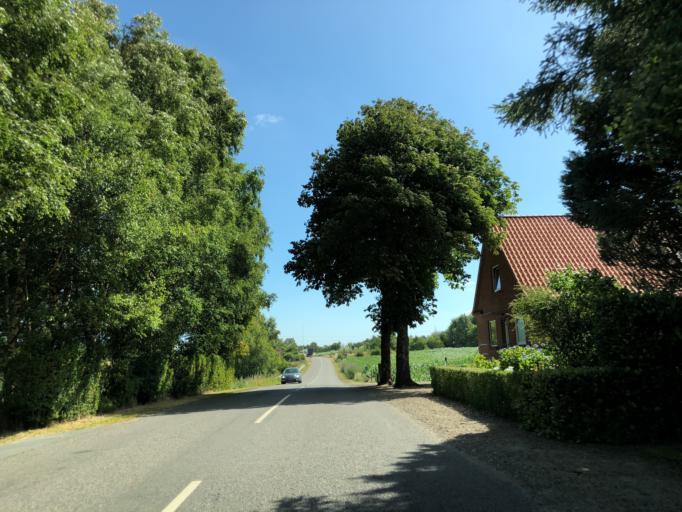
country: DK
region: North Denmark
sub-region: Vesthimmerland Kommune
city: Alestrup
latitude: 56.5749
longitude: 9.5476
